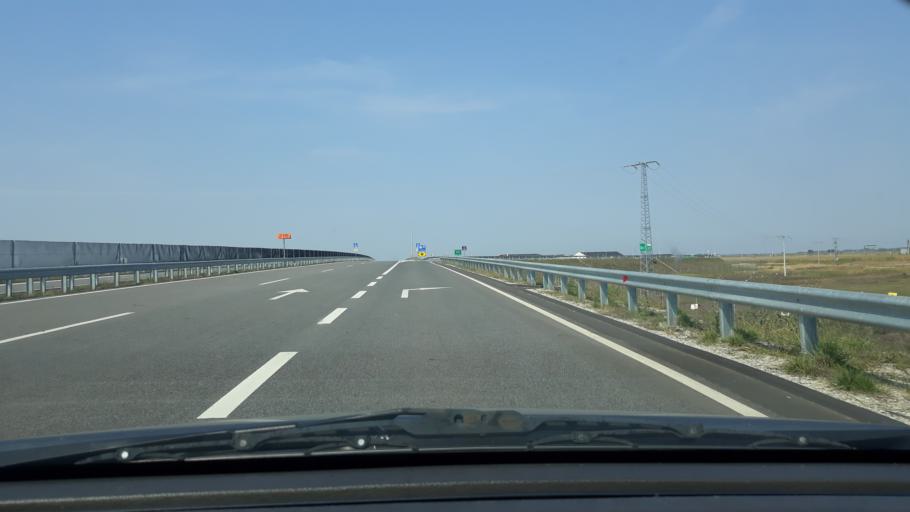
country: HU
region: Hajdu-Bihar
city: Berettyoujfalu
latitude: 47.2727
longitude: 21.5525
